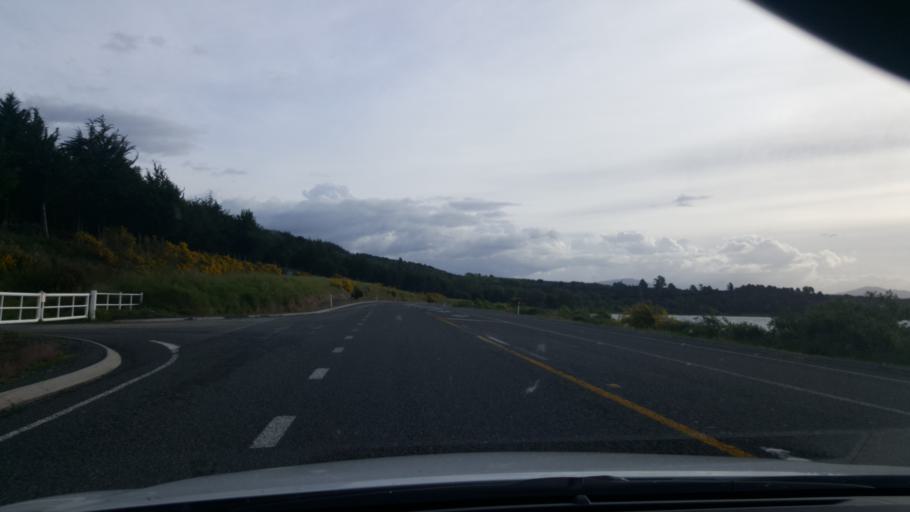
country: NZ
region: Waikato
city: Turangi
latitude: -38.9001
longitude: 175.9445
